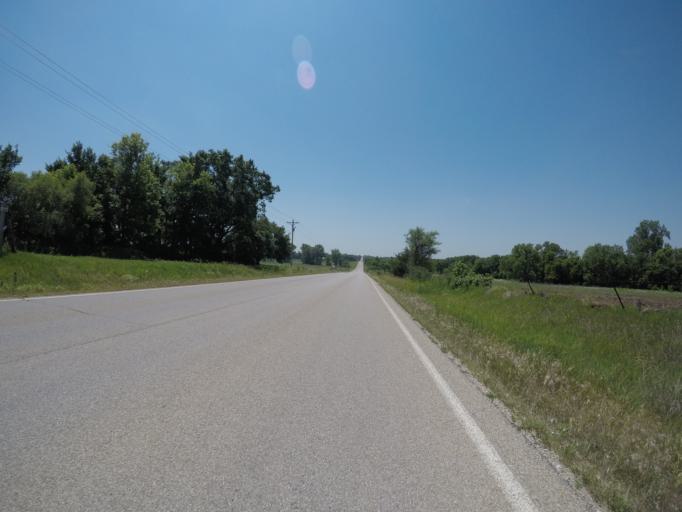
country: US
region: Kansas
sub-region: Pottawatomie County
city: Westmoreland
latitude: 39.2538
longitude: -96.4451
